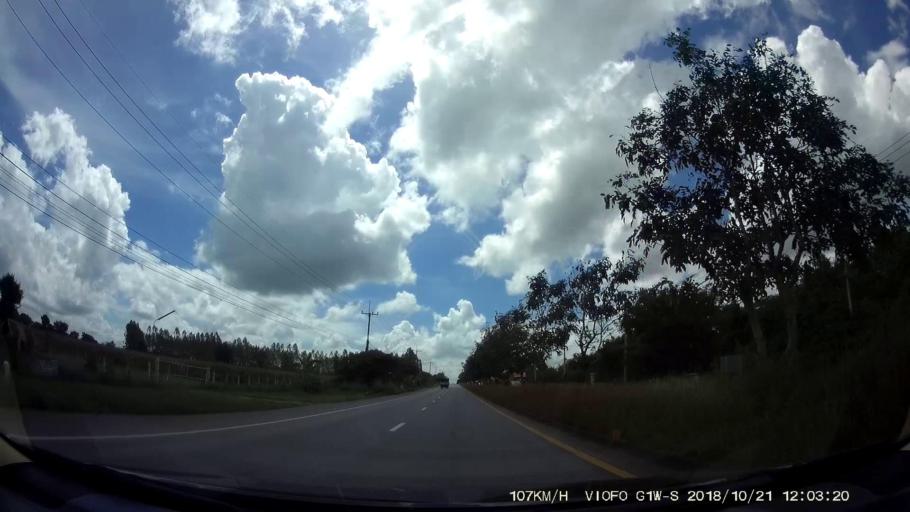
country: TH
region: Chaiyaphum
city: Chatturat
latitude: 15.5108
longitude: 101.8228
